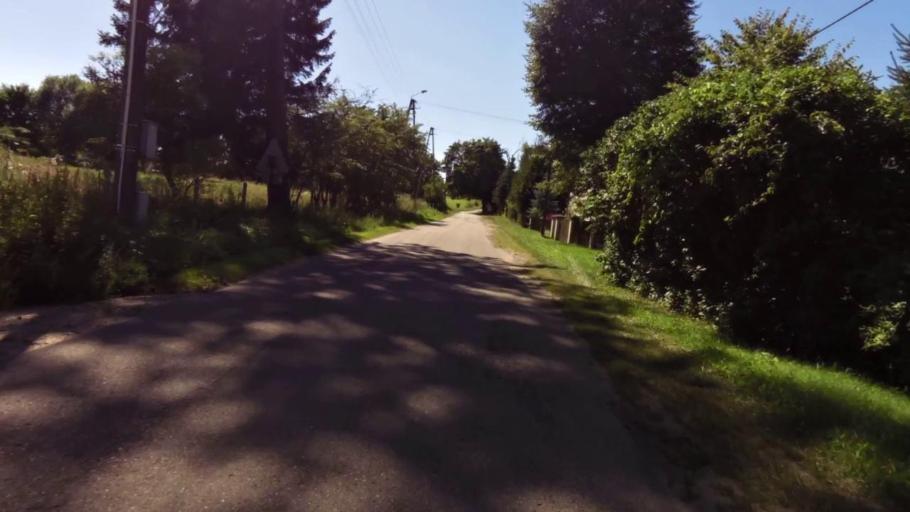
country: PL
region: West Pomeranian Voivodeship
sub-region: Powiat szczecinecki
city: Bialy Bor
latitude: 53.8728
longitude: 16.7962
